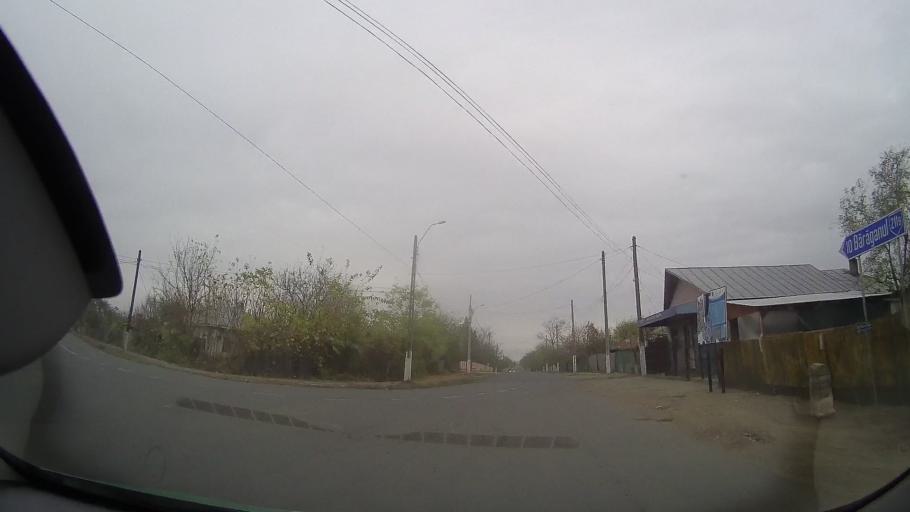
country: RO
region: Braila
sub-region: Comuna Budesti
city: Tataru
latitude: 44.8440
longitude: 27.4263
